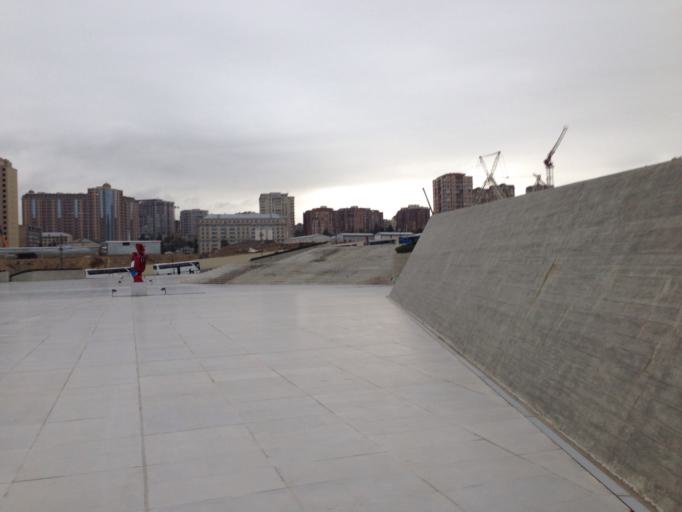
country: AZ
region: Baki
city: Baku
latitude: 40.3937
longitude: 49.8665
